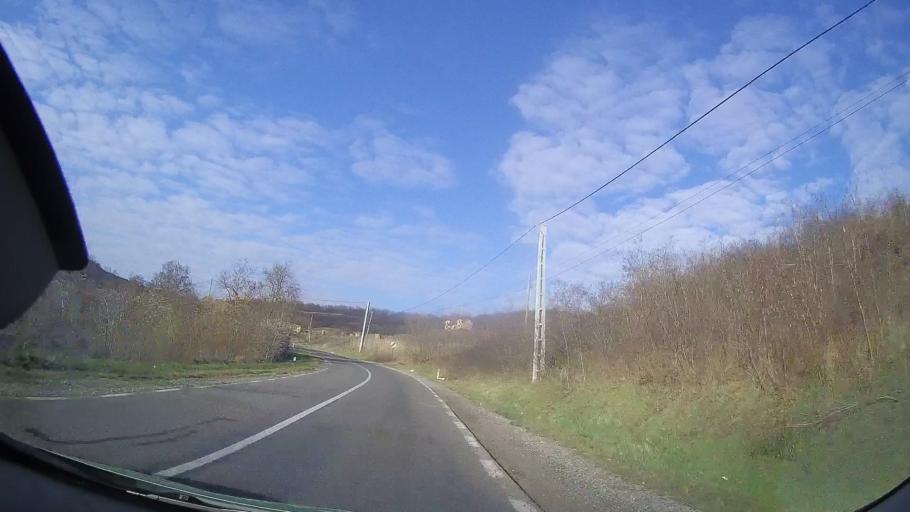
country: RO
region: Cluj
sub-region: Comuna Cojocna
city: Cojocna
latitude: 46.8076
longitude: 23.8404
